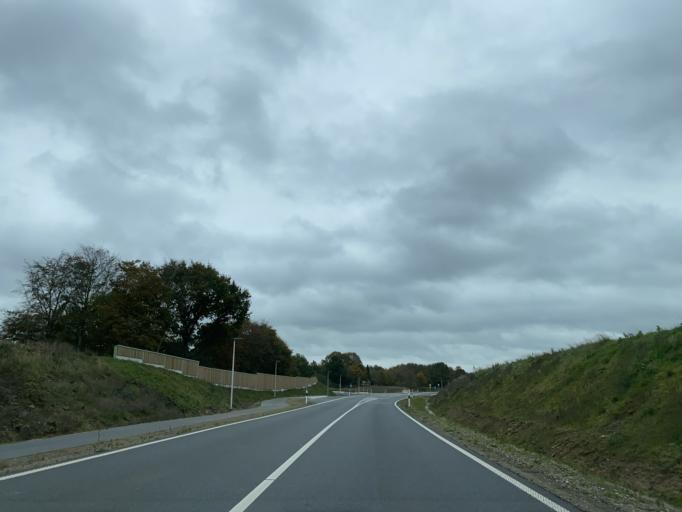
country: DE
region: Schleswig-Holstein
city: Tastrup
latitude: 54.7776
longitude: 9.4876
